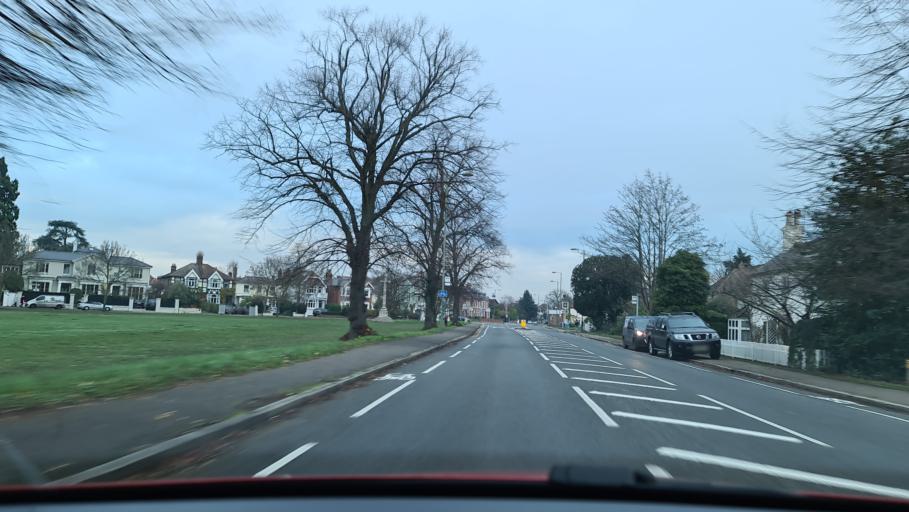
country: GB
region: England
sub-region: Surrey
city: Thames Ditton
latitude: 51.3858
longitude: -0.3311
